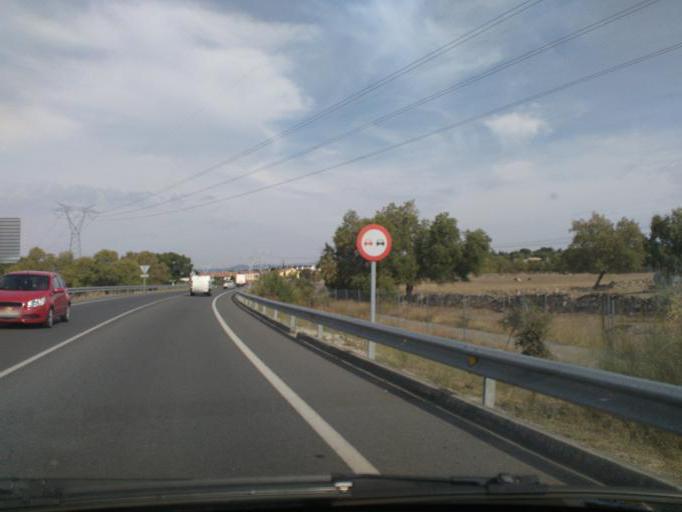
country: ES
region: Madrid
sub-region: Provincia de Madrid
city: Galapagar
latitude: 40.5783
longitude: -3.9908
